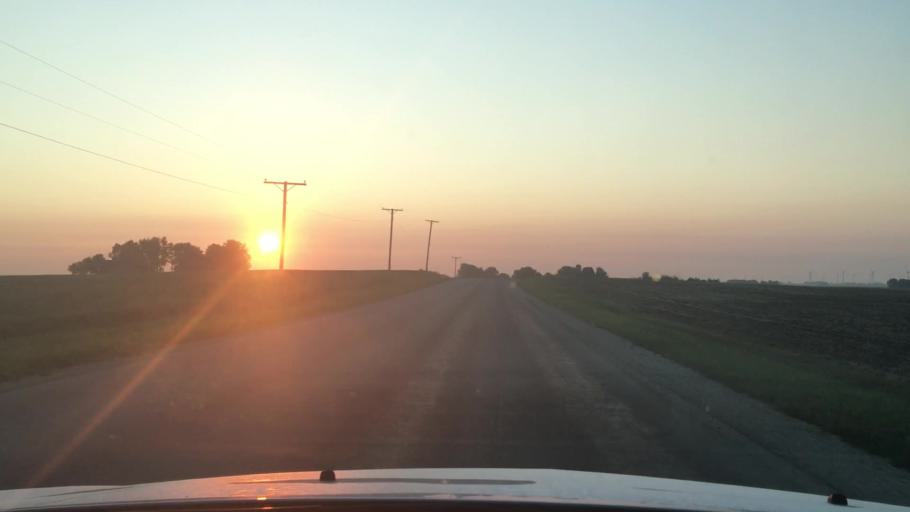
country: US
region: Illinois
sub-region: DeKalb County
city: Malta
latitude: 41.8488
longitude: -88.8855
